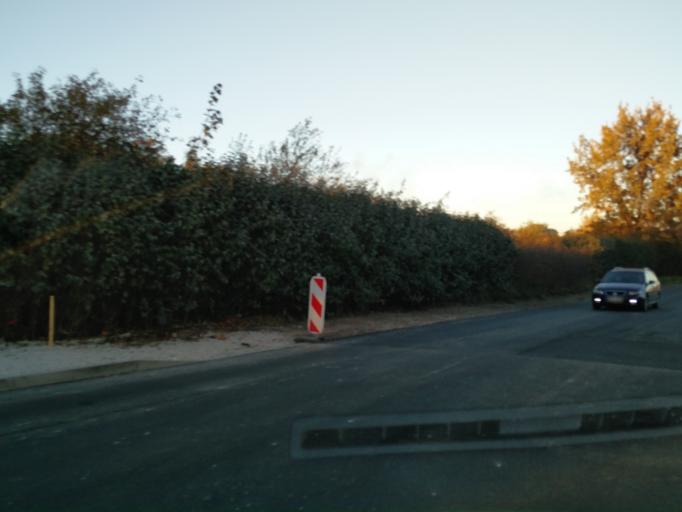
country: EE
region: Tartu
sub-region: Tartu linn
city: Tartu
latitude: 58.3549
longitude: 26.7084
